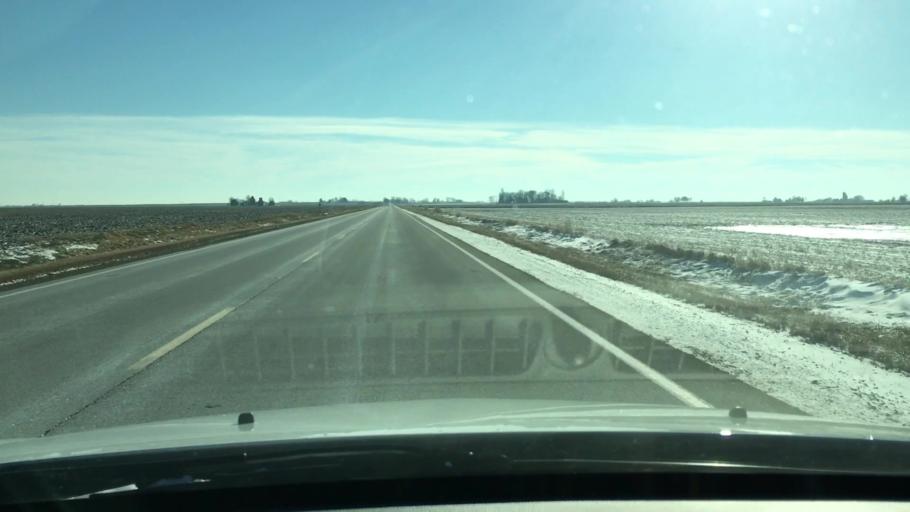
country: US
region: Illinois
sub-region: Ogle County
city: Rochelle
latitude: 41.8606
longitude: -89.0732
